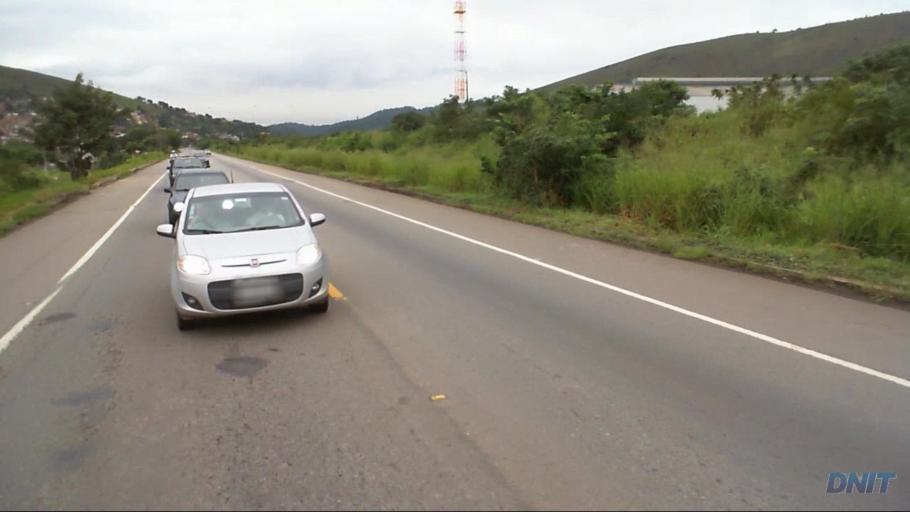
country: BR
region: Minas Gerais
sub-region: Coronel Fabriciano
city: Coronel Fabriciano
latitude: -19.5303
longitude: -42.6098
